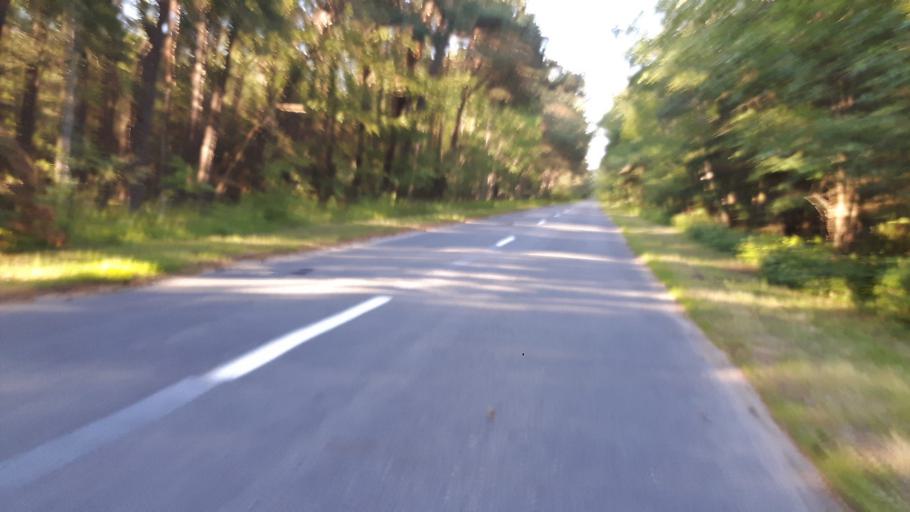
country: LT
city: Nida
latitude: 55.2386
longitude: 20.9119
